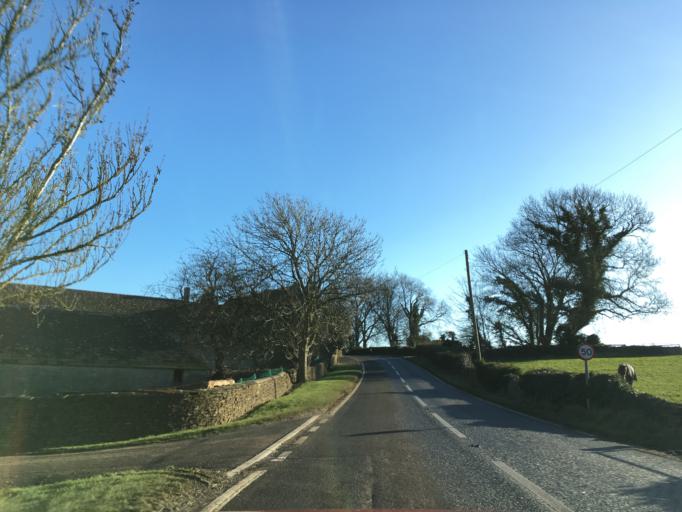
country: GB
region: England
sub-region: Wiltshire
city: Nettleton
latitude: 51.5265
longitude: -2.3082
